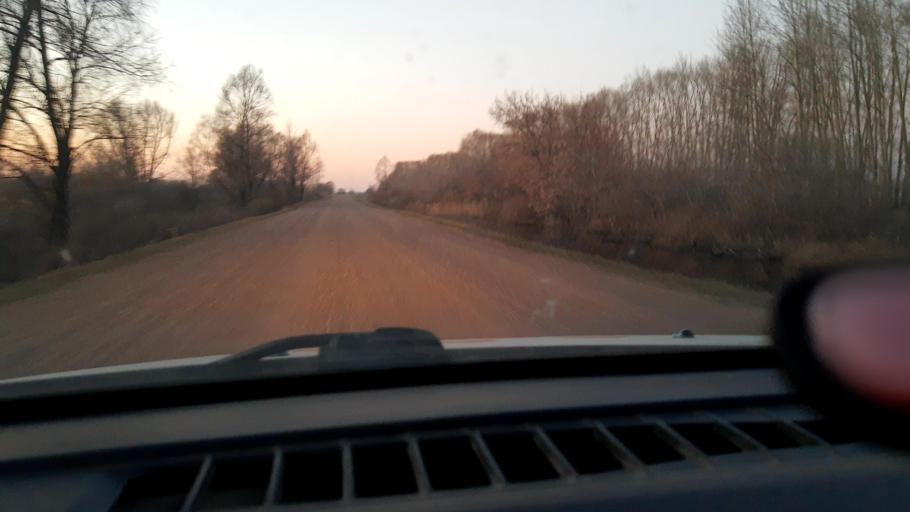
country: RU
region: Bashkortostan
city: Asanovo
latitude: 54.8634
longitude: 55.4627
